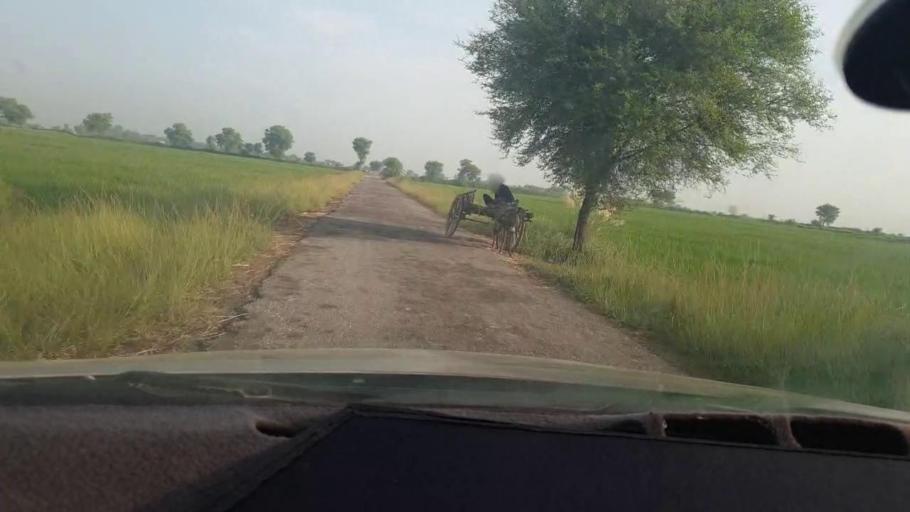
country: PK
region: Sindh
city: Jacobabad
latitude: 28.3010
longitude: 68.4152
